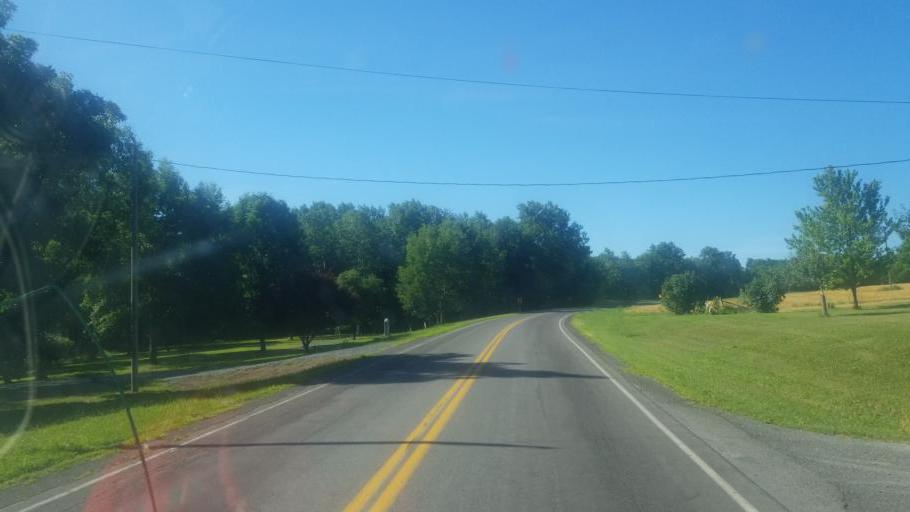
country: US
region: New York
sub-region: Ontario County
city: Clifton Springs
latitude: 42.8466
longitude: -77.1086
